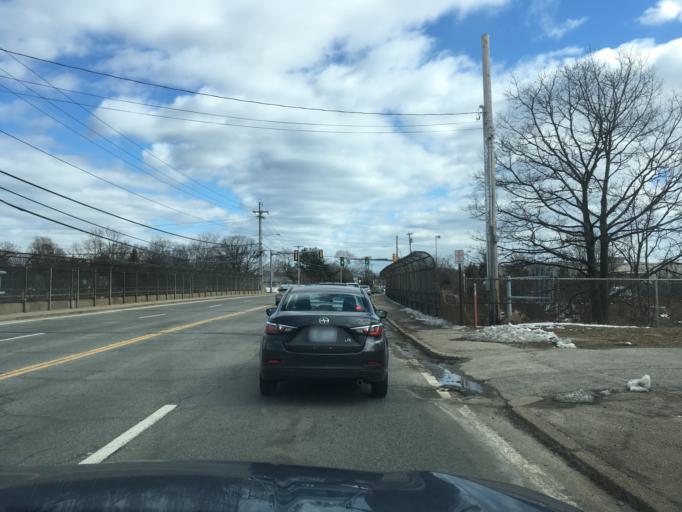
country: US
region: Rhode Island
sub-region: Kent County
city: Warwick
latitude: 41.7226
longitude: -71.4675
